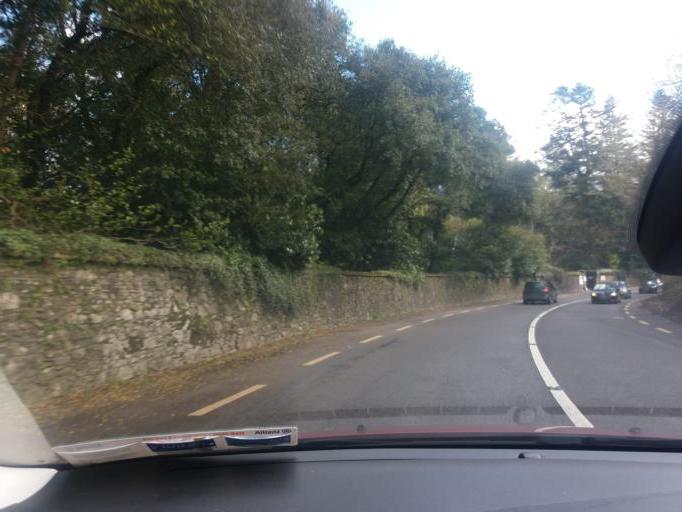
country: IE
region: Munster
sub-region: County Cork
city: Cobh
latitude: 51.8912
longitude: -8.3018
